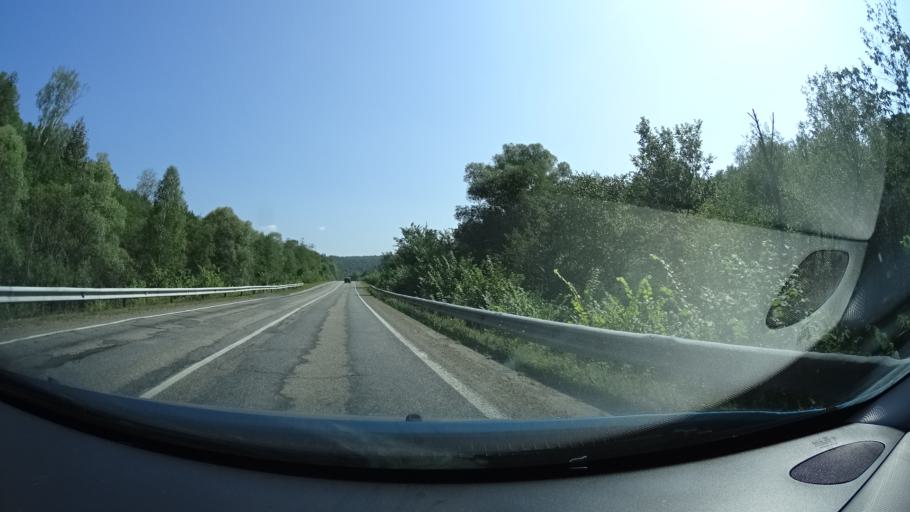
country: RU
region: Bashkortostan
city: Inzer
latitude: 54.3374
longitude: 57.1100
